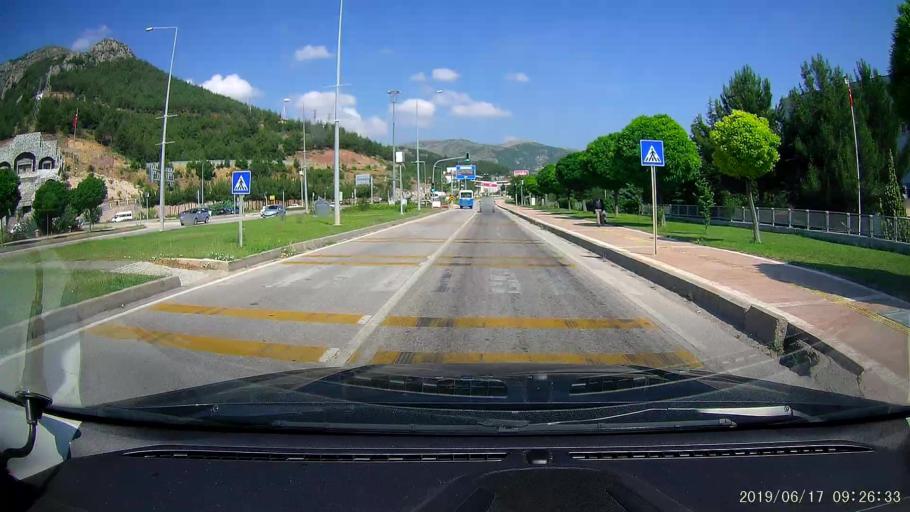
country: TR
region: Amasya
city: Amasya
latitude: 40.6700
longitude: 35.8346
